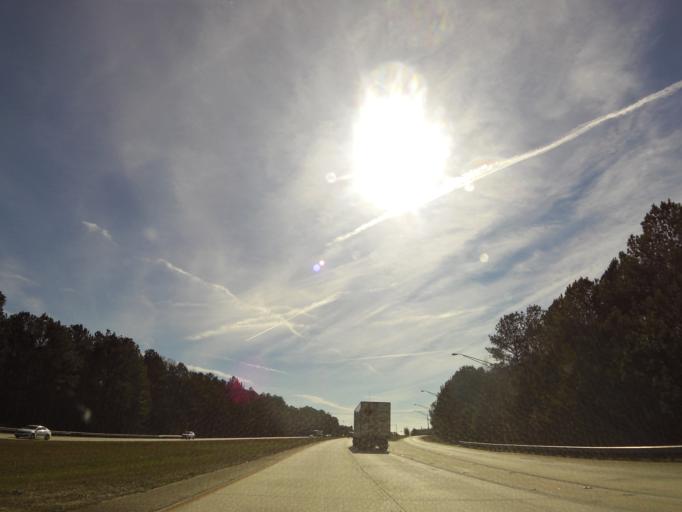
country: US
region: Georgia
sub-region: Troup County
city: Hogansville
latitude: 33.0917
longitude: -84.9111
